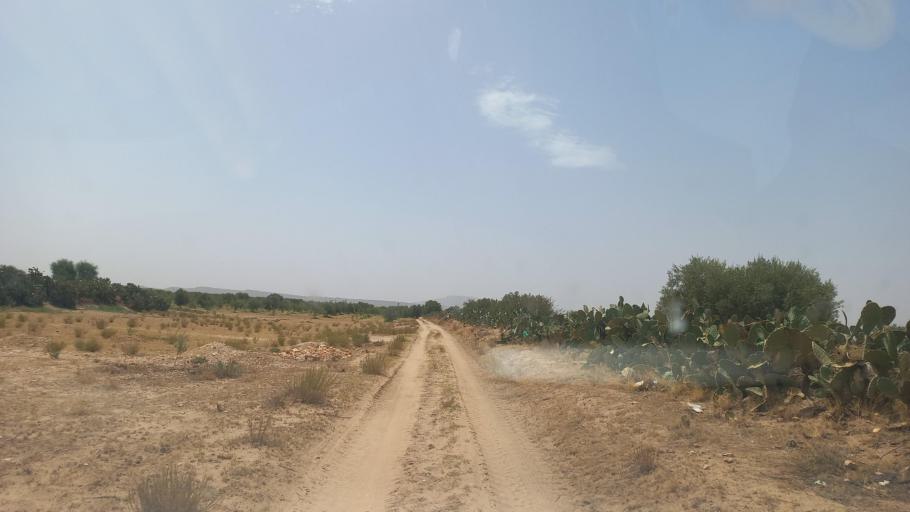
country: TN
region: Al Qasrayn
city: Kasserine
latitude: 35.2628
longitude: 9.0059
